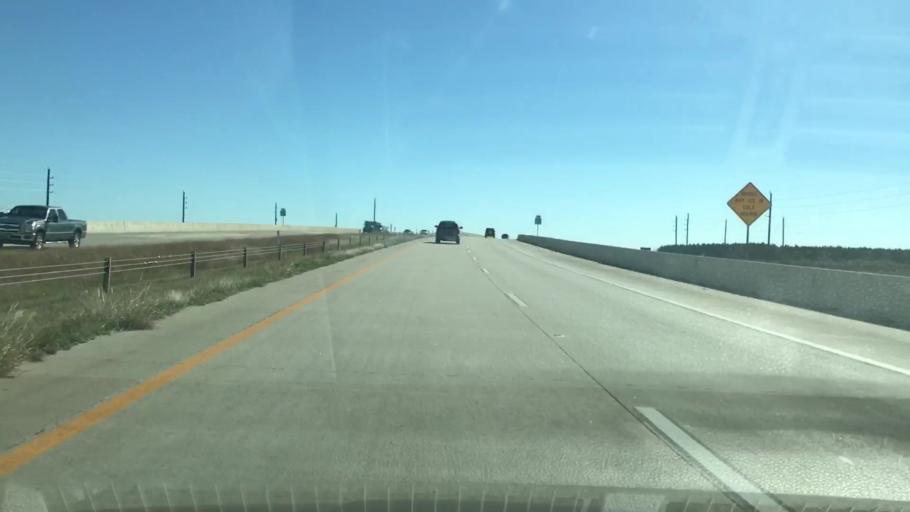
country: US
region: Texas
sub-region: Harris County
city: Cypress
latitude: 29.9068
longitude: -95.7594
